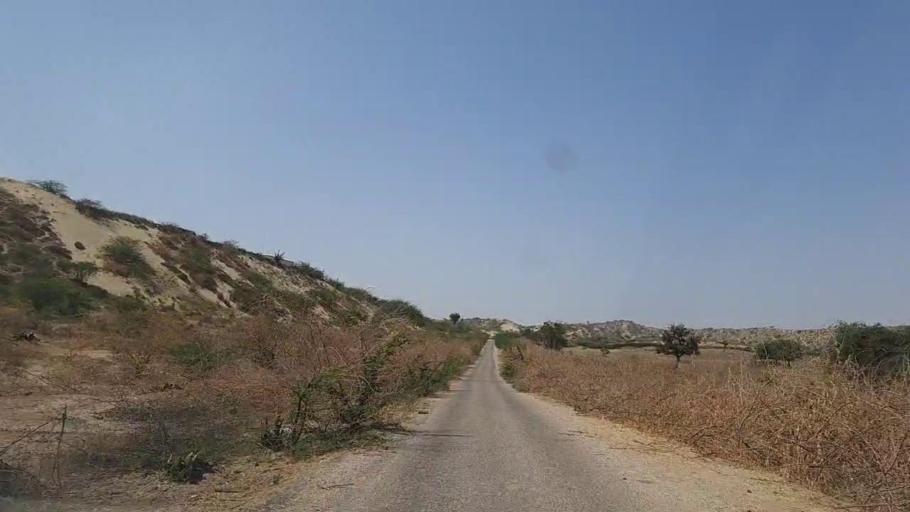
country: PK
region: Sindh
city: Diplo
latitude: 24.5258
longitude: 69.3699
